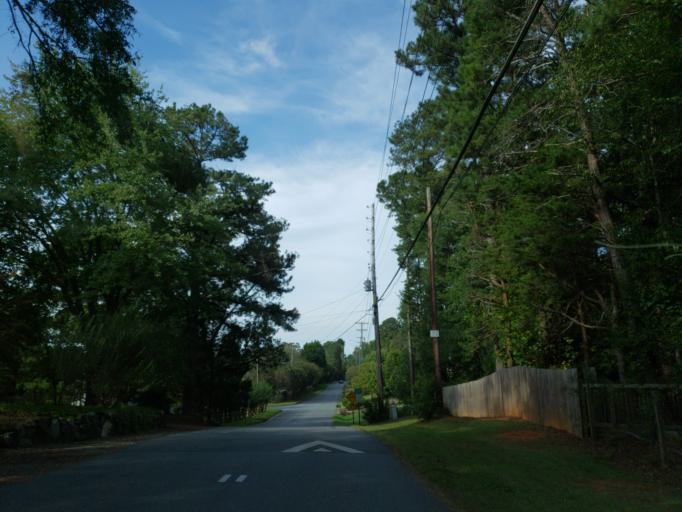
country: US
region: Georgia
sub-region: Cherokee County
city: Woodstock
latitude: 34.0747
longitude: -84.4980
